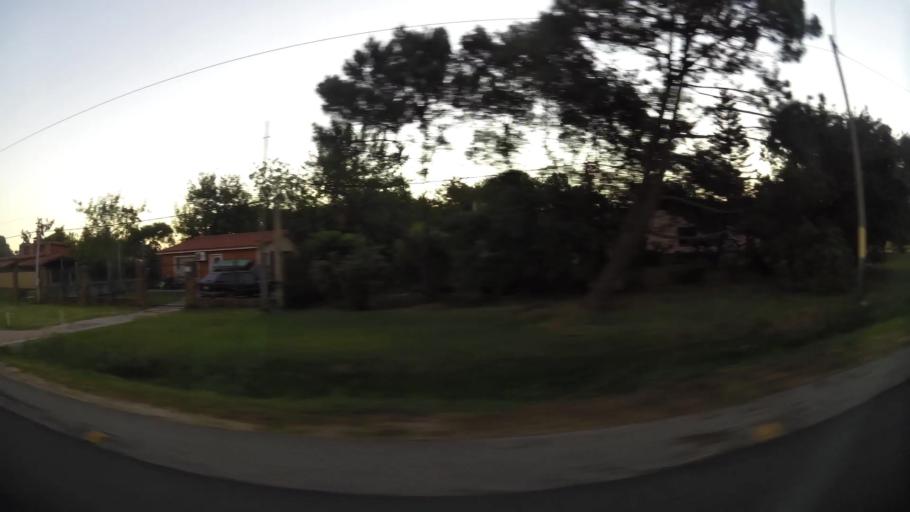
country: UY
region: Canelones
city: Barra de Carrasco
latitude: -34.8261
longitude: -55.9435
